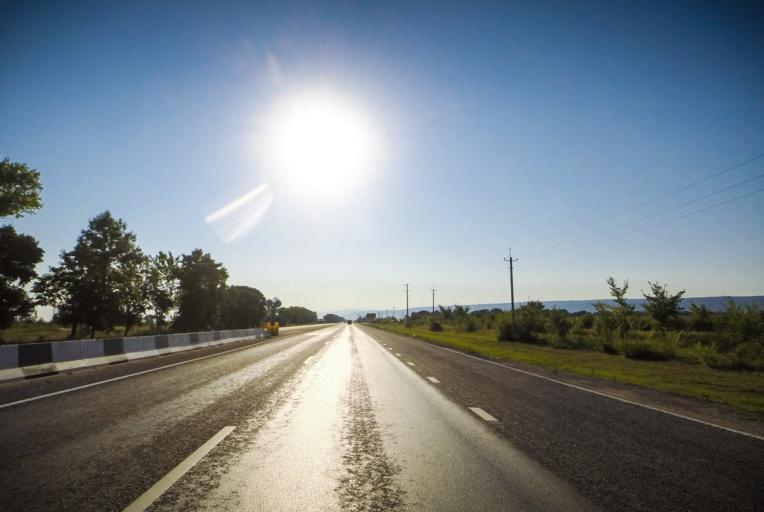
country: RU
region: Kabardino-Balkariya
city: Urukh
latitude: 43.3217
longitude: 44.0723
